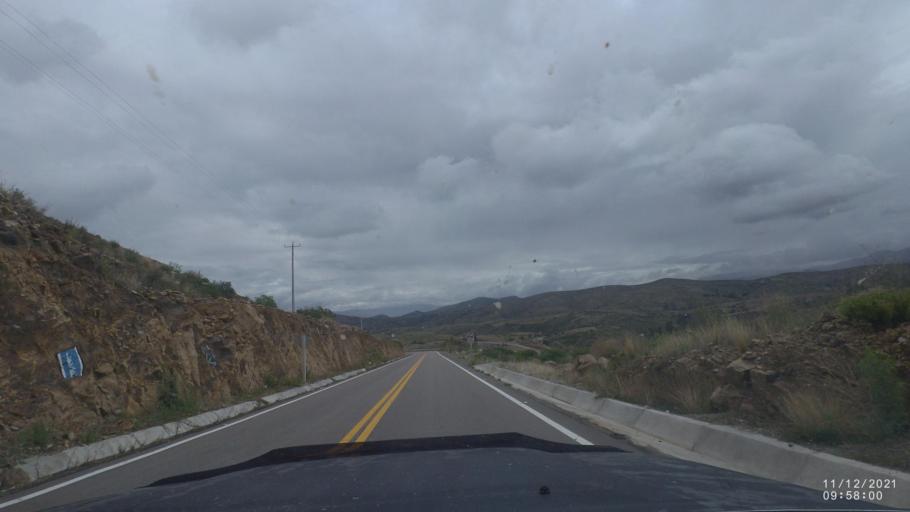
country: BO
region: Cochabamba
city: Cliza
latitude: -17.7541
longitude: -65.9198
